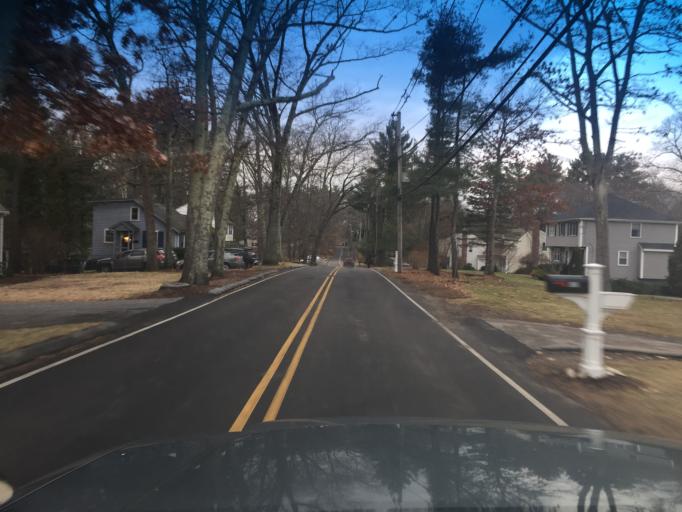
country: US
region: Massachusetts
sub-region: Norfolk County
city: Millis
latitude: 42.1761
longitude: -71.3642
